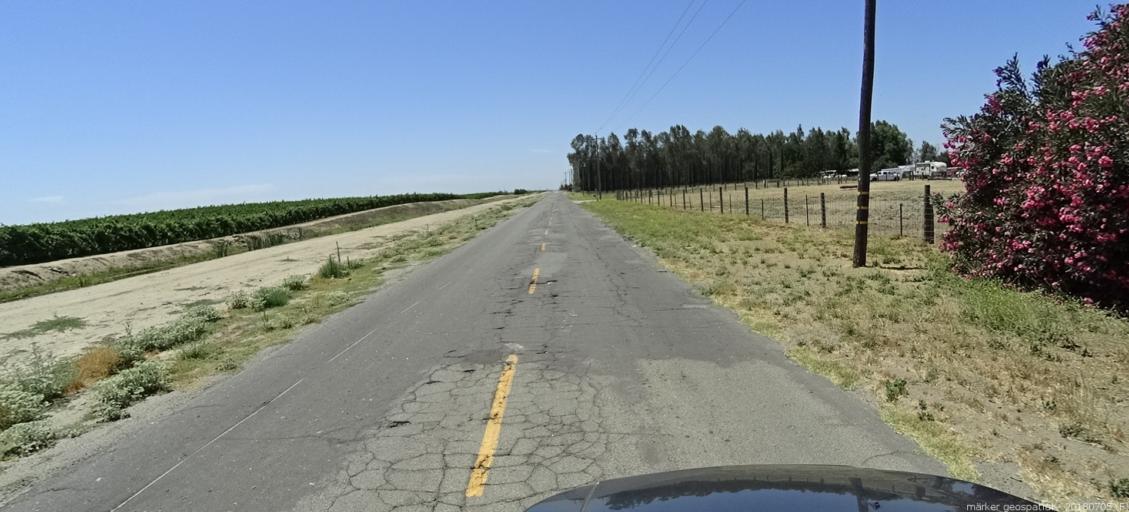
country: US
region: California
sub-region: Madera County
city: Fairmead
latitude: 37.1197
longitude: -120.2021
